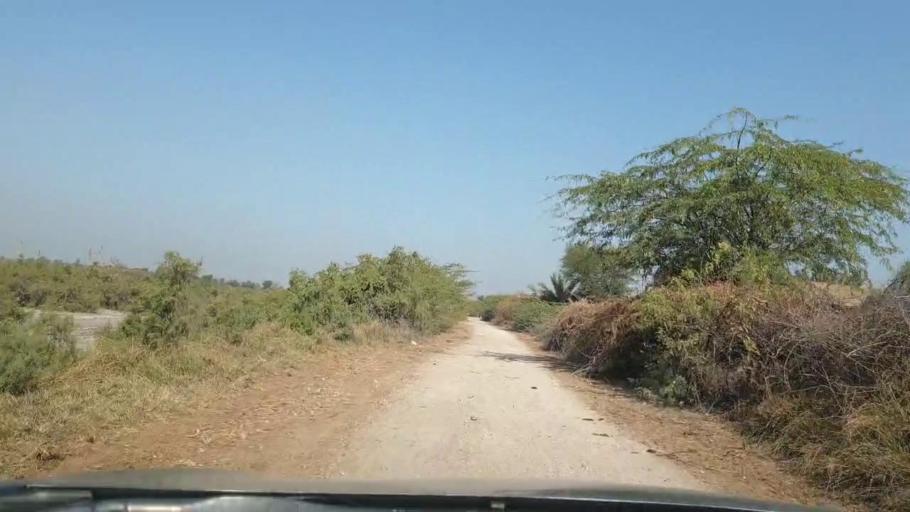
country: PK
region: Sindh
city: Berani
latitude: 25.6779
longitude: 68.8962
